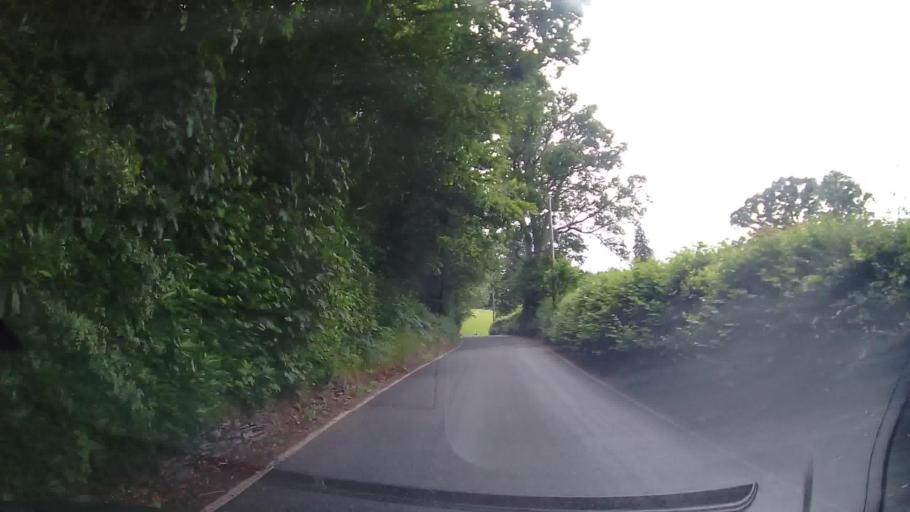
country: GB
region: Wales
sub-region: Conwy
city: Llangwm
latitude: 52.9159
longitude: -3.5117
